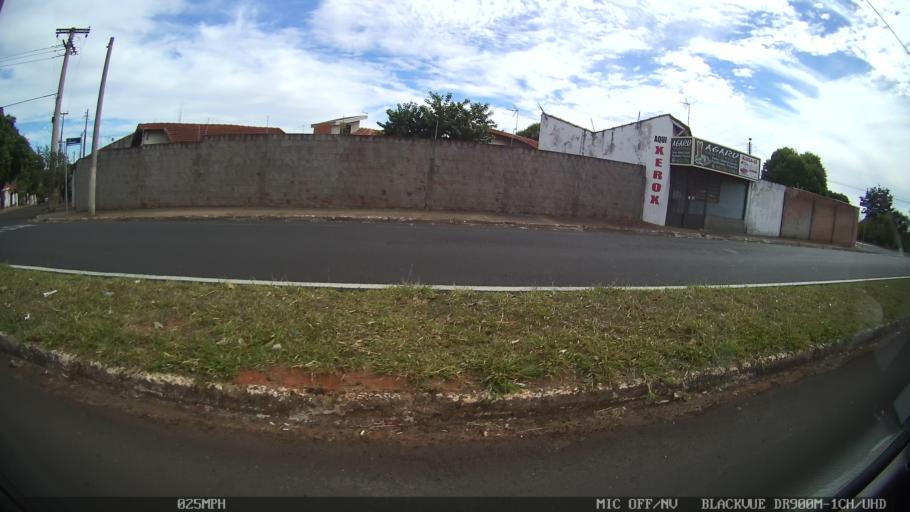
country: BR
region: Sao Paulo
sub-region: Catanduva
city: Catanduva
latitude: -21.1455
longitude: -48.9463
